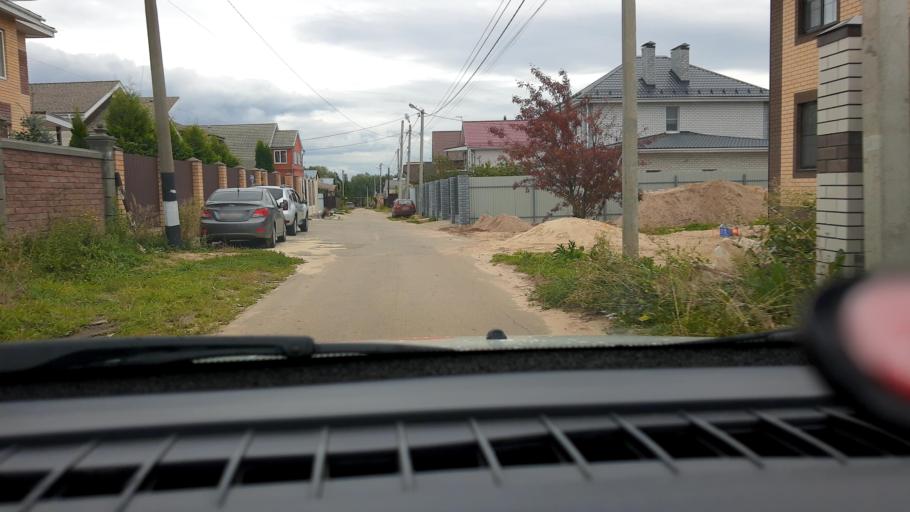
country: RU
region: Nizjnij Novgorod
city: Afonino
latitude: 56.2044
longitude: 44.1006
